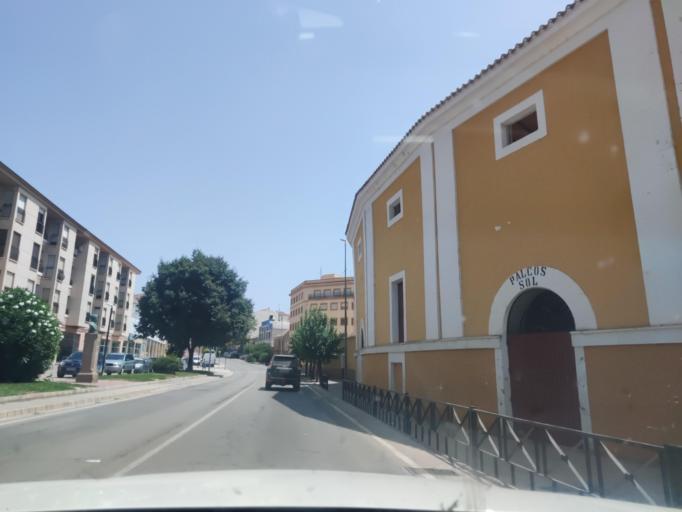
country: ES
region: Castille-La Mancha
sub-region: Provincia de Albacete
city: Hellin
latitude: 38.5110
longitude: -1.6961
